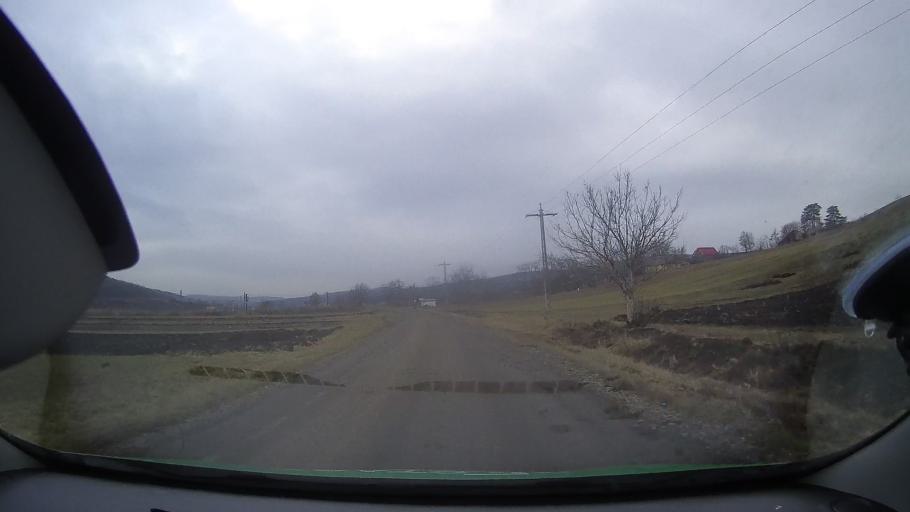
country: RO
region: Mures
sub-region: Comuna Bichis
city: Bichis
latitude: 46.3853
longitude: 24.0802
